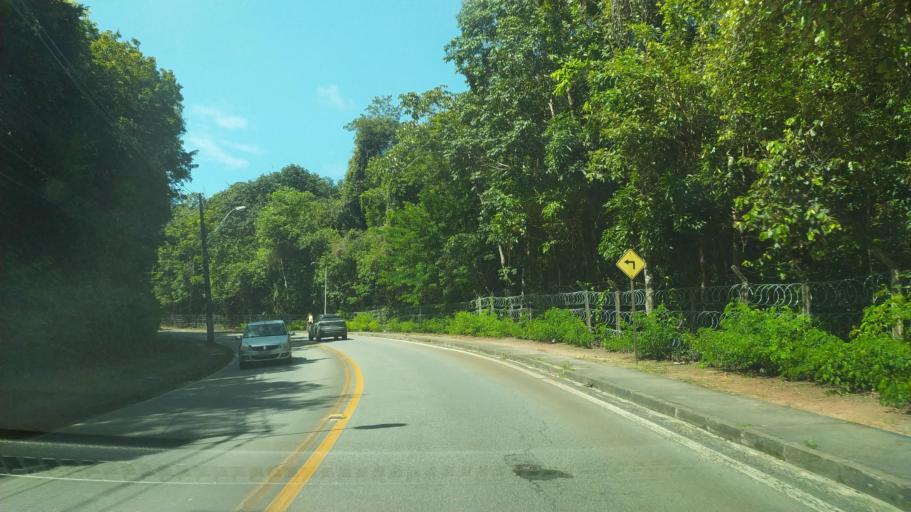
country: BR
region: Alagoas
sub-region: Maceio
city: Maceio
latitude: -9.5982
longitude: -35.7385
